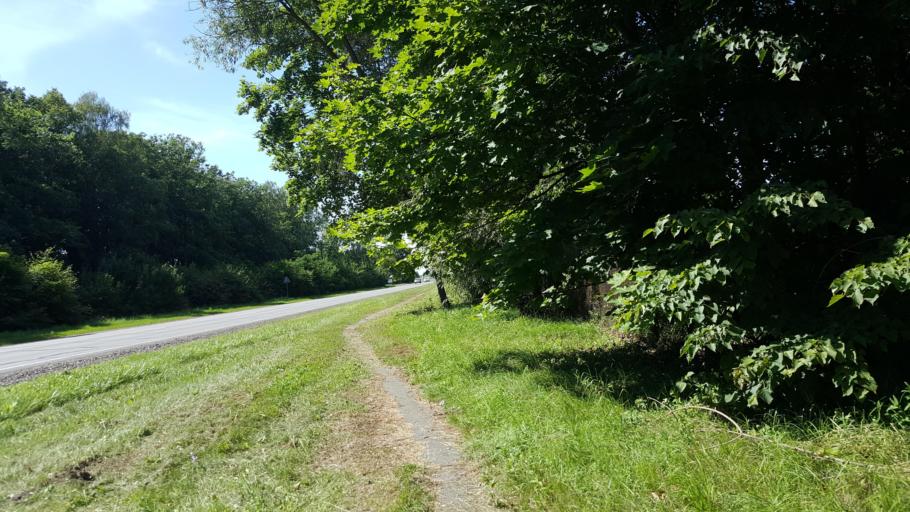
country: BY
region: Brest
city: Charnawchytsy
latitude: 52.2646
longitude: 23.7645
